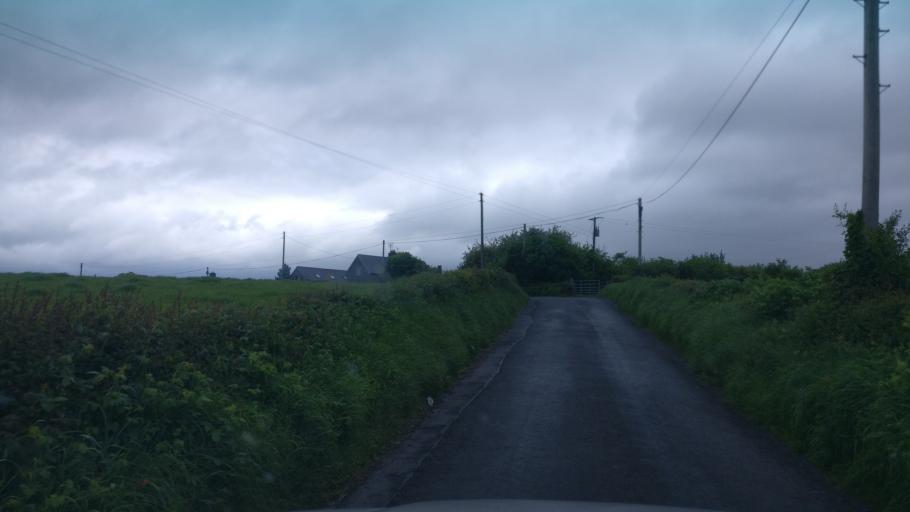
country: IE
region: Connaught
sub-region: County Galway
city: Portumna
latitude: 53.1440
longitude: -8.2873
